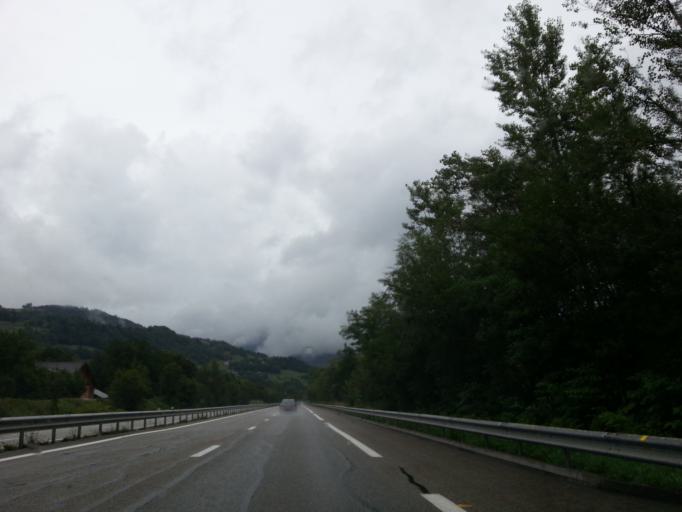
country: FR
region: Rhone-Alpes
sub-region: Departement de la Savoie
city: Marthod
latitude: 45.7155
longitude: 6.4083
